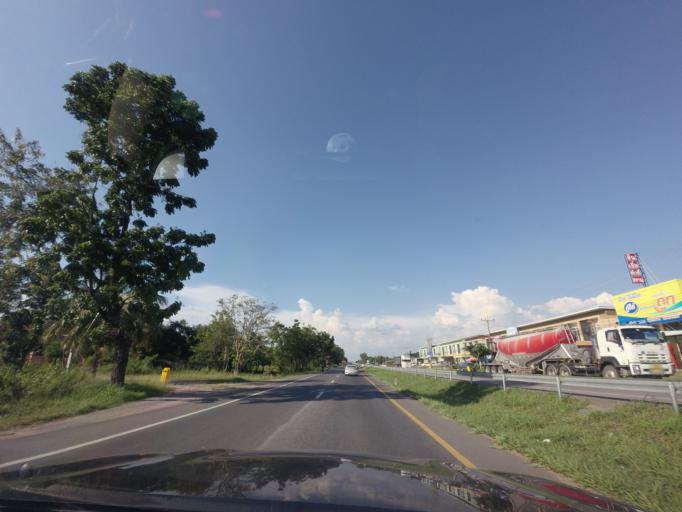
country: TH
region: Khon Kaen
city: Non Sila
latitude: 15.9695
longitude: 102.6923
